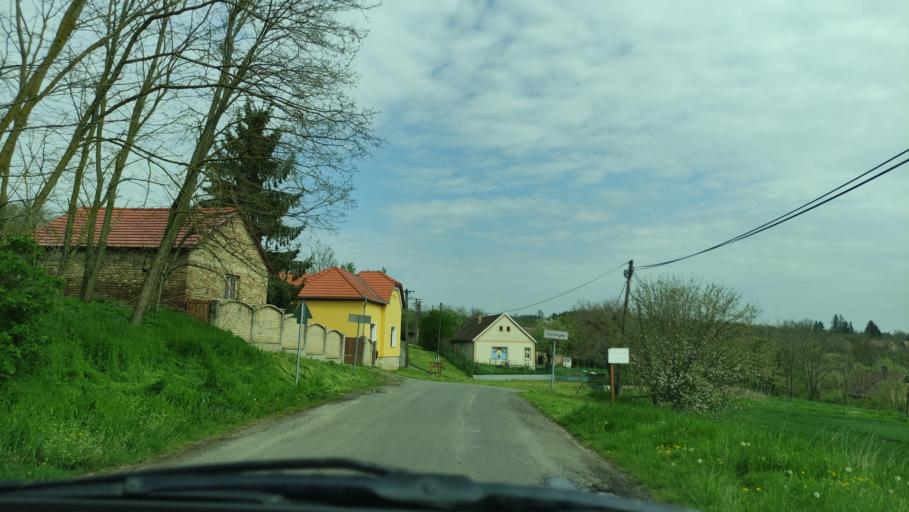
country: HU
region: Baranya
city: Magocs
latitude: 46.3032
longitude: 18.1782
